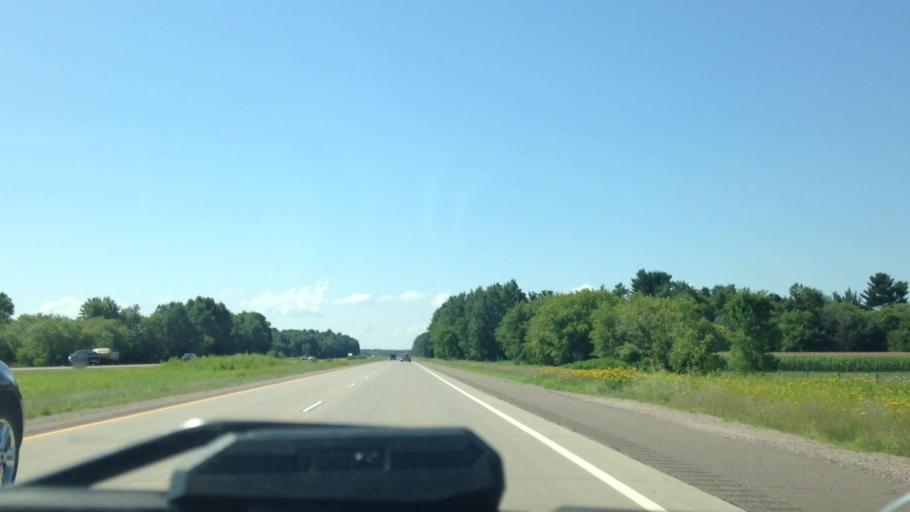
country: US
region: Wisconsin
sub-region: Barron County
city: Cameron
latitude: 45.4361
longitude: -91.7610
